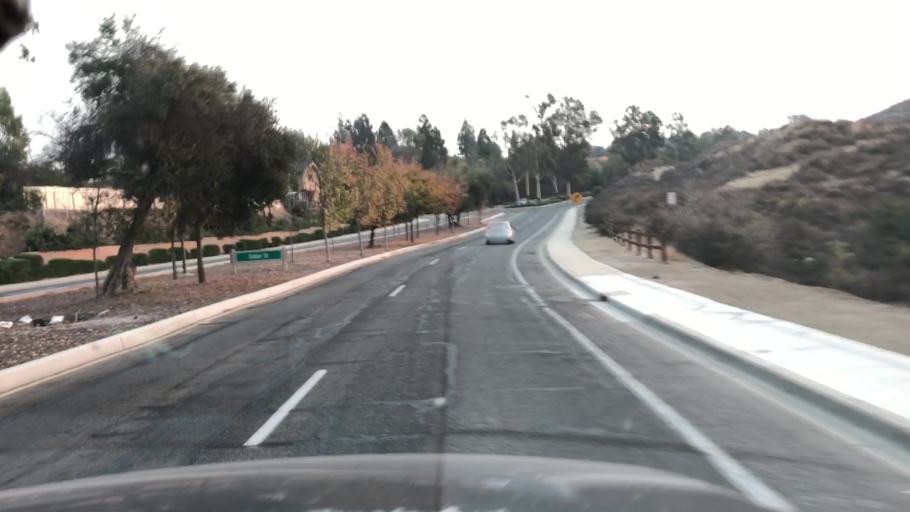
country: US
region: California
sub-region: Ventura County
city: Thousand Oaks
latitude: 34.2111
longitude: -118.8862
